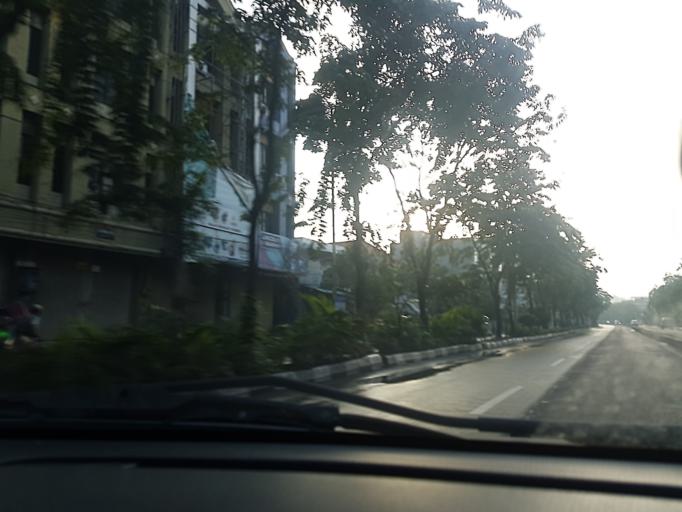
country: ID
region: East Java
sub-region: Kota Surabaya
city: Surabaya
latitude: -7.2451
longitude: 112.7239
